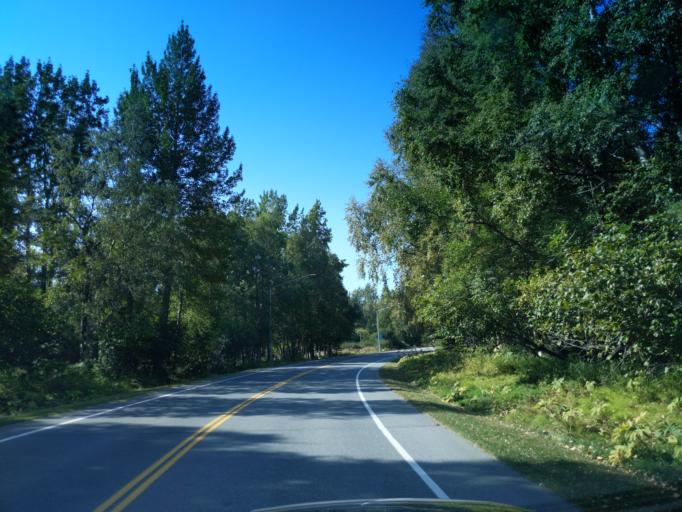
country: US
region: Alaska
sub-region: Anchorage Municipality
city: Anchorage
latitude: 61.1531
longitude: -150.0202
